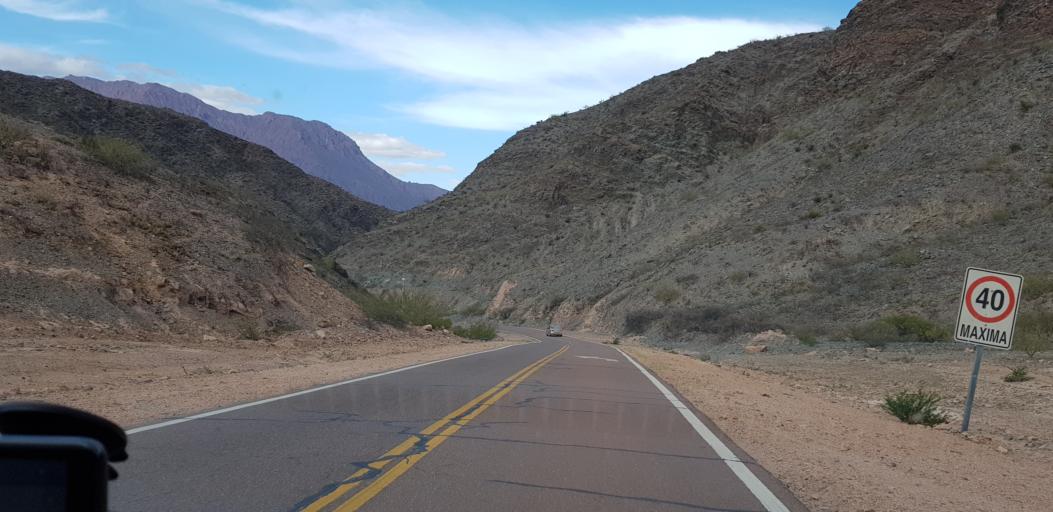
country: AR
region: Salta
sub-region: Cafayete
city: Cafayate
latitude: -26.0264
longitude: -65.8425
